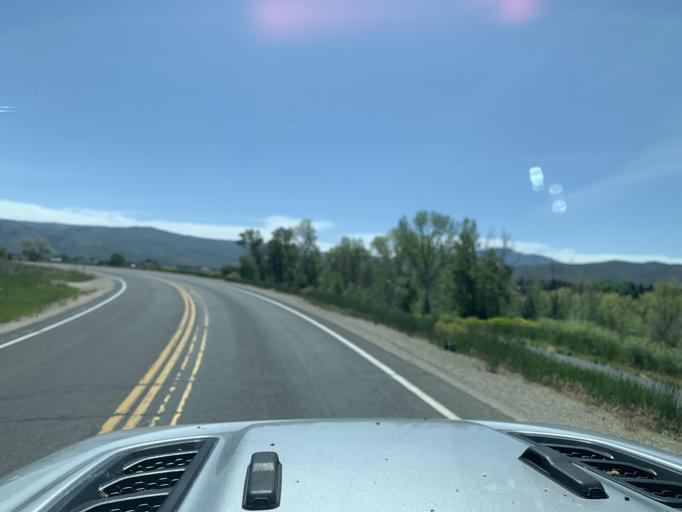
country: US
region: Utah
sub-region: Weber County
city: Wolf Creek
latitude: 41.2679
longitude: -111.7757
